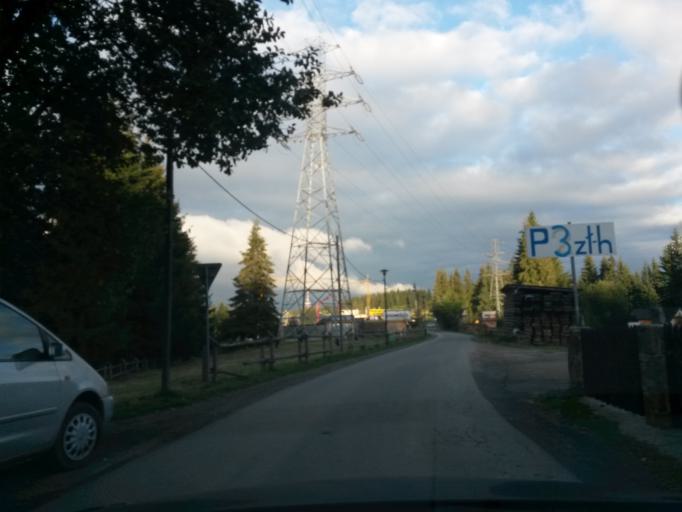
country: PL
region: Lesser Poland Voivodeship
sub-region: Powiat tatrzanski
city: Koscielisko
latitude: 49.3037
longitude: 19.9117
